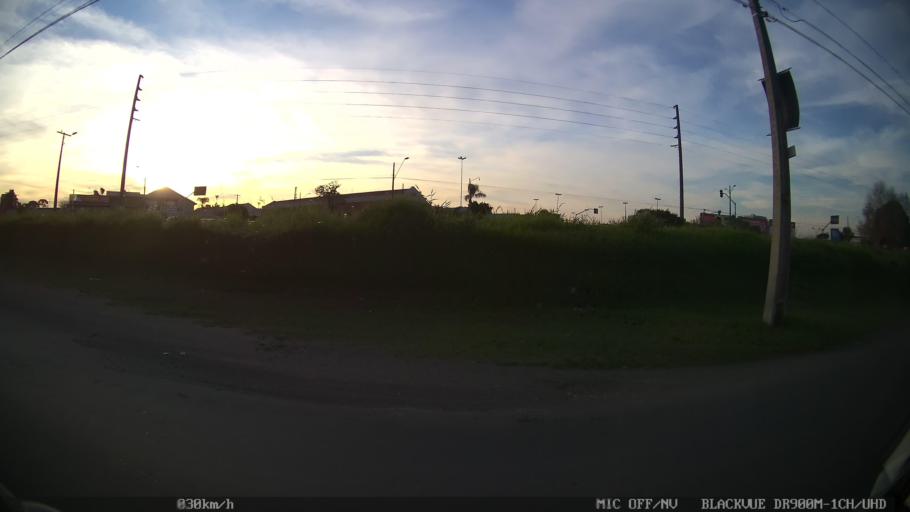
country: BR
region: Parana
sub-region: Pinhais
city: Pinhais
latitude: -25.4414
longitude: -49.1817
